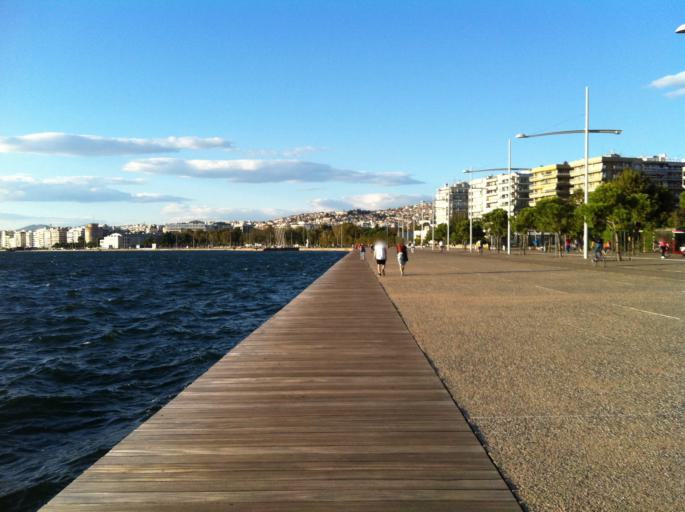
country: GR
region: Central Macedonia
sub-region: Nomos Thessalonikis
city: Agios Pavlos
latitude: 40.6184
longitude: 22.9516
